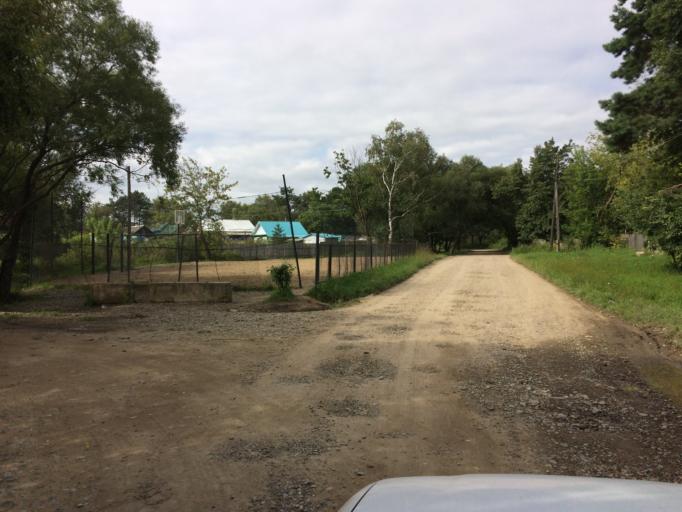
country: RU
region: Primorskiy
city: Dal'nerechensk
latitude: 45.9215
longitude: 133.7146
